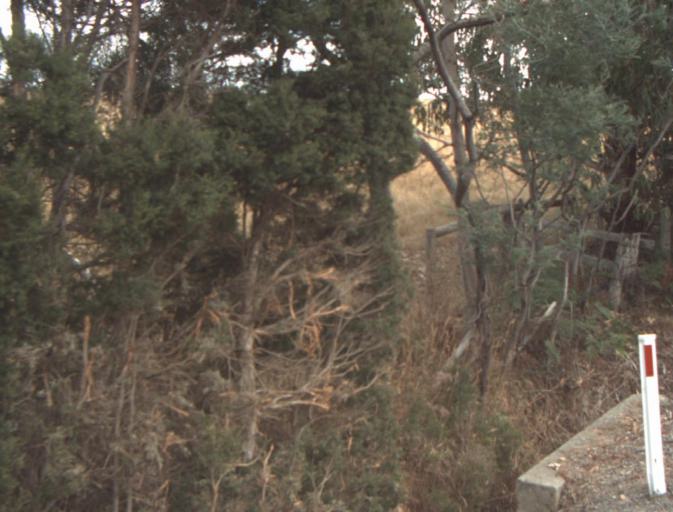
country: AU
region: Tasmania
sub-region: Launceston
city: Mayfield
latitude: -41.2938
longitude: 147.0241
